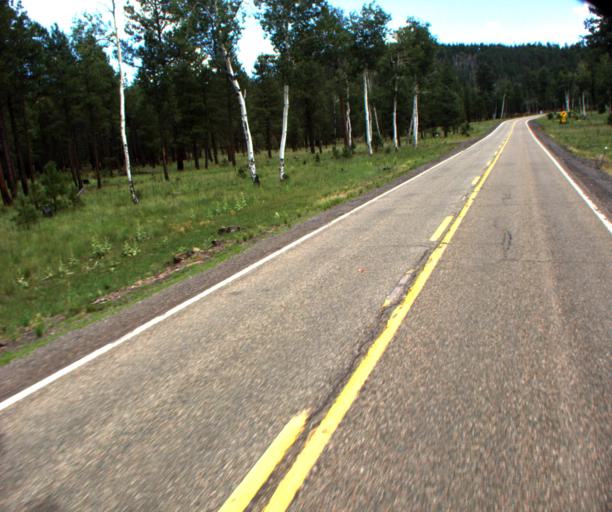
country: US
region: Arizona
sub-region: Coconino County
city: Flagstaff
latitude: 35.3274
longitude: -111.7754
